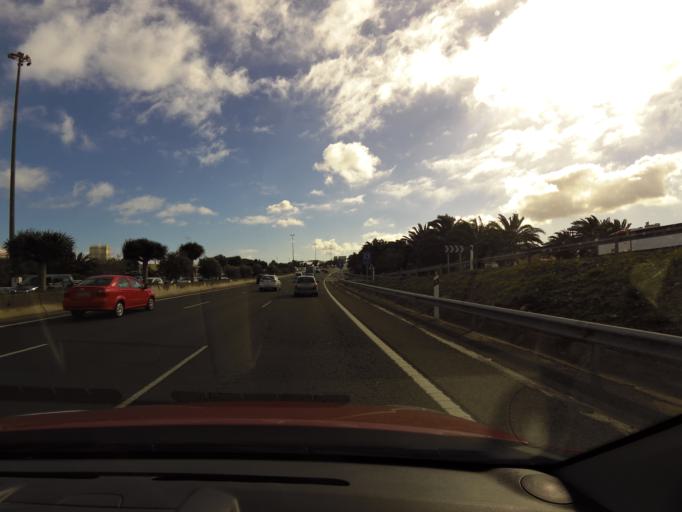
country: ES
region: Canary Islands
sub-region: Provincia de Las Palmas
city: Telde
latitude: 27.9496
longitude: -15.3874
